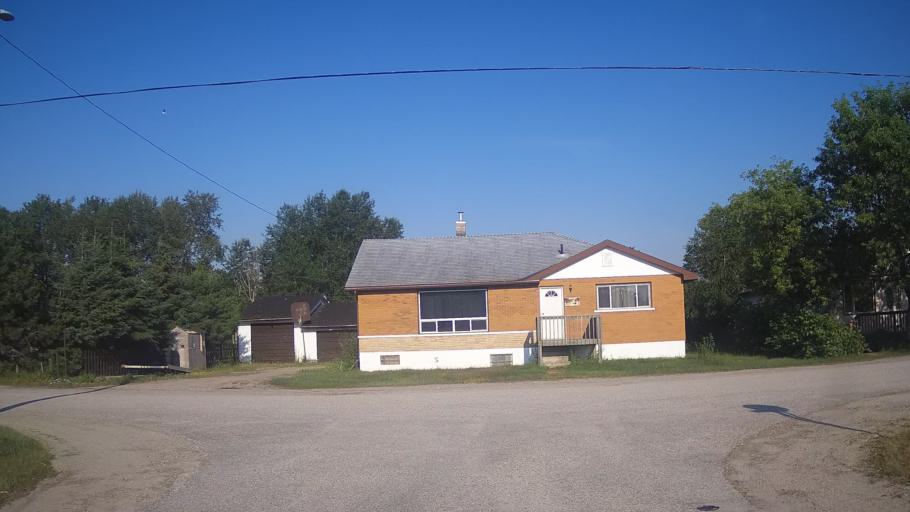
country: CA
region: Ontario
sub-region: Rainy River District
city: Atikokan
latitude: 49.4174
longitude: -91.6636
